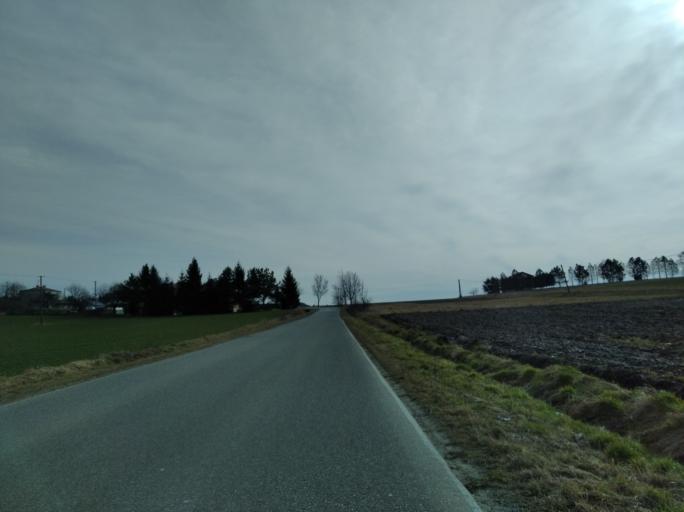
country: PL
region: Subcarpathian Voivodeship
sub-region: Powiat brzozowski
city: Orzechowka
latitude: 49.7206
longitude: 21.9632
